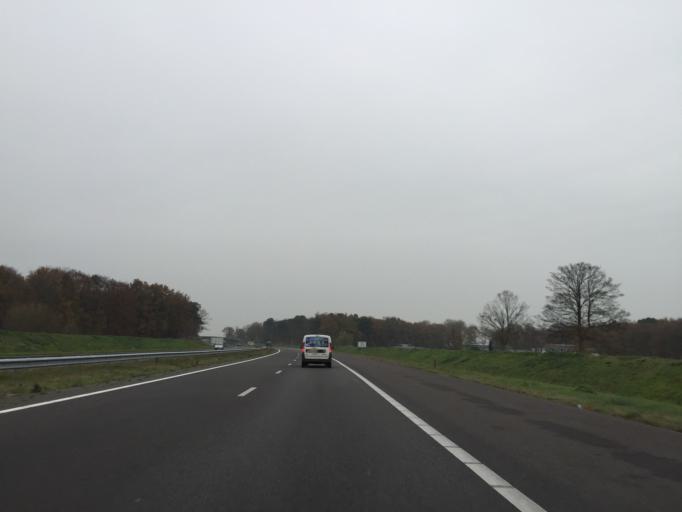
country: NL
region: North Brabant
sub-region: Gemeente Bergen op Zoom
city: Bergen op Zoom
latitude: 51.5209
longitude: 4.3115
